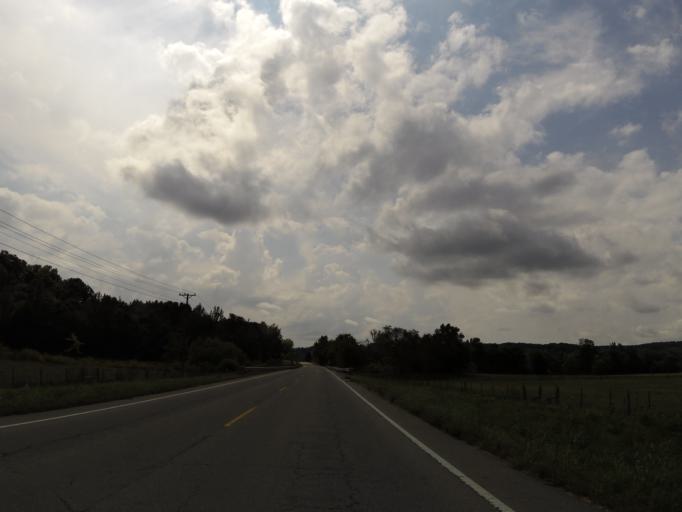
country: US
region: Tennessee
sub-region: Perry County
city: Linden
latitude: 35.8206
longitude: -87.7835
